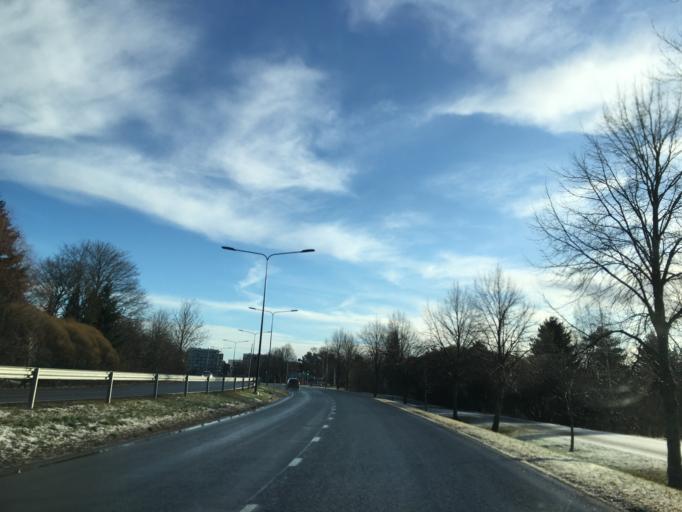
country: FI
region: Varsinais-Suomi
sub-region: Turku
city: Raisio
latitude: 60.4719
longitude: 22.2118
